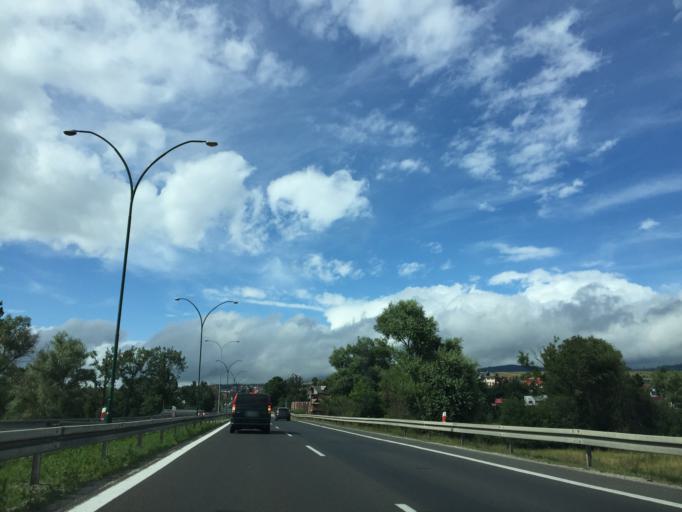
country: PL
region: Lesser Poland Voivodeship
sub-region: Powiat nowotarski
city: Nowy Targ
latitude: 49.4843
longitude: 20.0199
